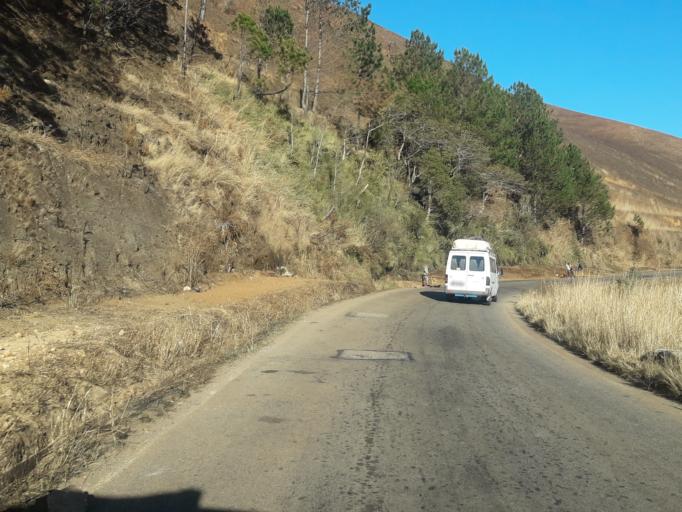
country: MG
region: Analamanga
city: Ankazobe
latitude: -17.9261
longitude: 47.1060
